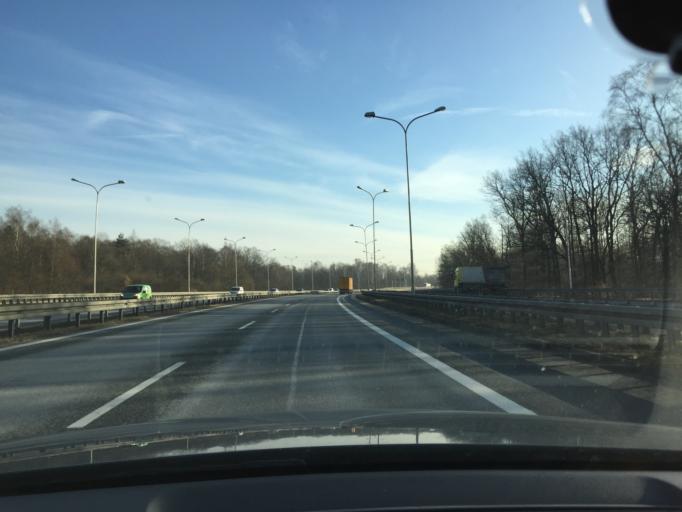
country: PL
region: Silesian Voivodeship
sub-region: Katowice
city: Katowice
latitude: 50.2403
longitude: 19.0559
